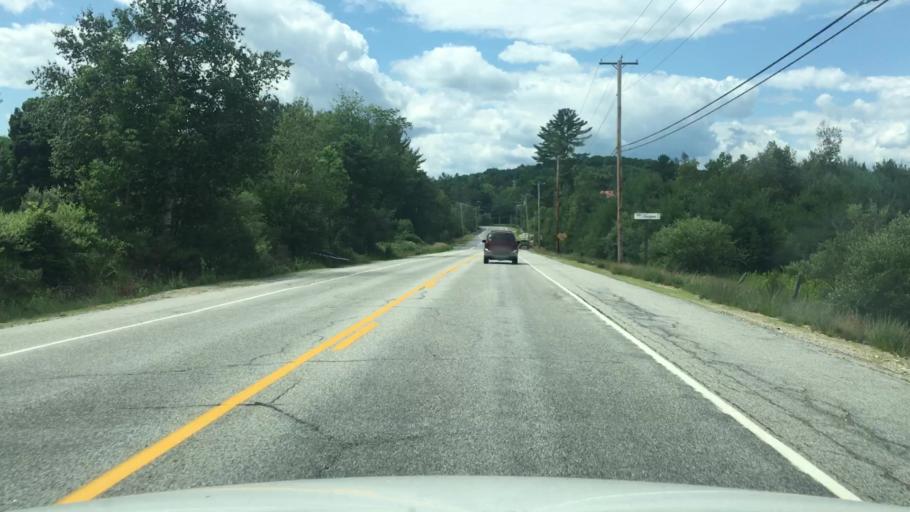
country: US
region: Maine
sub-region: Oxford County
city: West Paris
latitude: 44.3841
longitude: -70.6245
